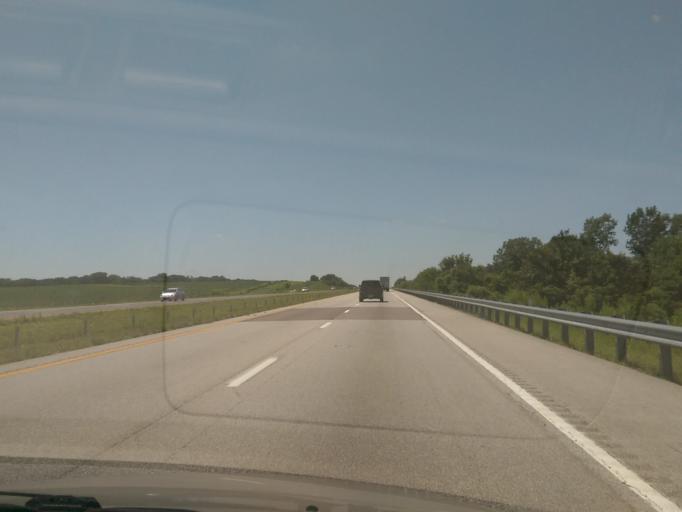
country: US
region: Missouri
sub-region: Cooper County
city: Boonville
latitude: 38.9345
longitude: -92.9233
